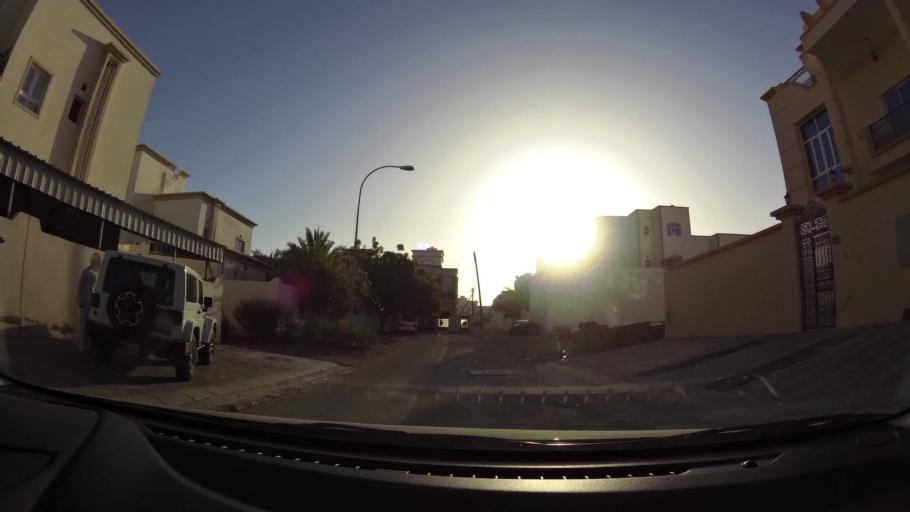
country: OM
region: Muhafazat Masqat
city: As Sib al Jadidah
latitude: 23.6099
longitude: 58.2302
